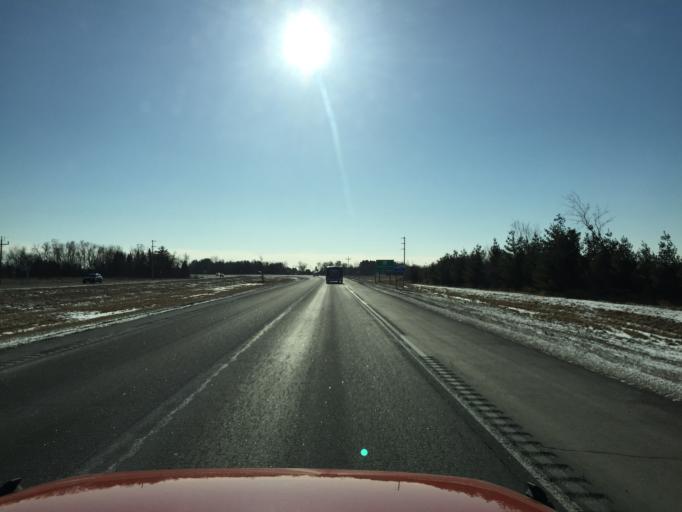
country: US
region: Minnesota
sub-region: Mille Lacs County
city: Milaca
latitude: 45.7920
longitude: -93.6546
